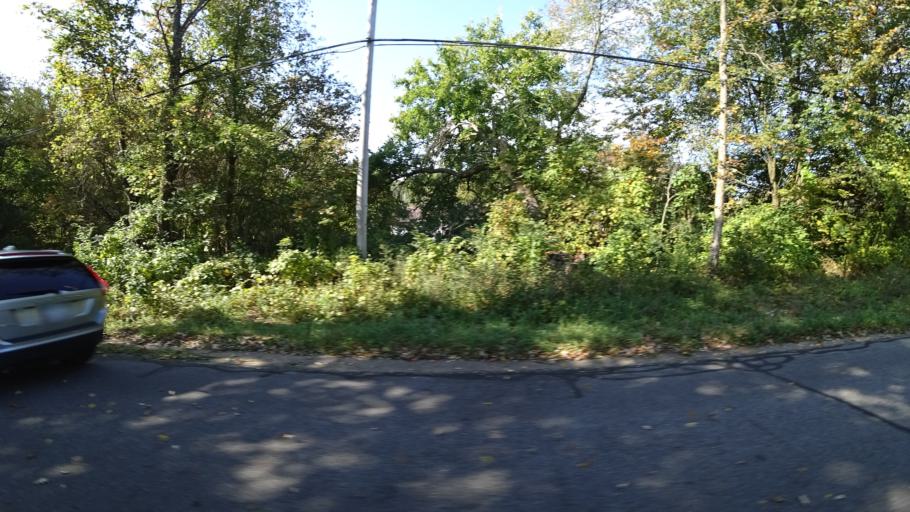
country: US
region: Michigan
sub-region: Saint Joseph County
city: Three Rivers
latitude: 41.9265
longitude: -85.6357
